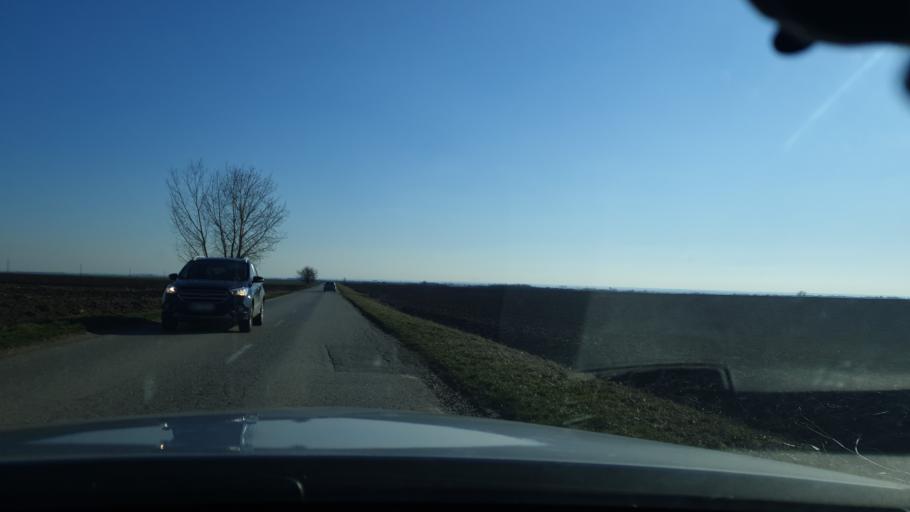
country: RS
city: Vrdnik
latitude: 45.0797
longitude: 19.8080
